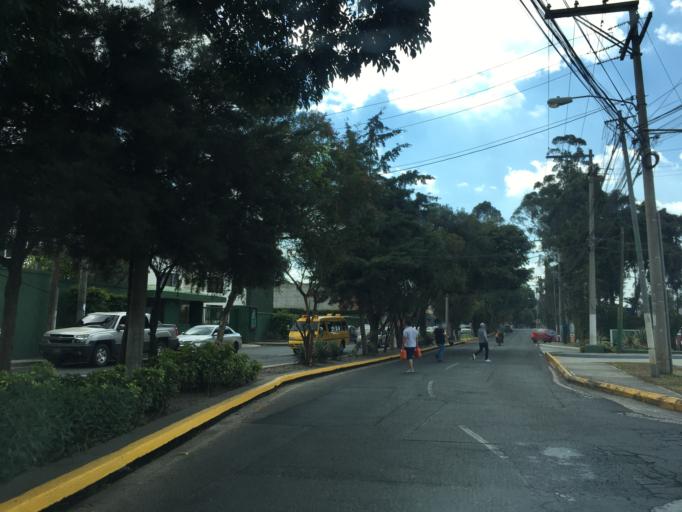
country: GT
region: Guatemala
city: Guatemala City
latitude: 14.6250
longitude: -90.4707
